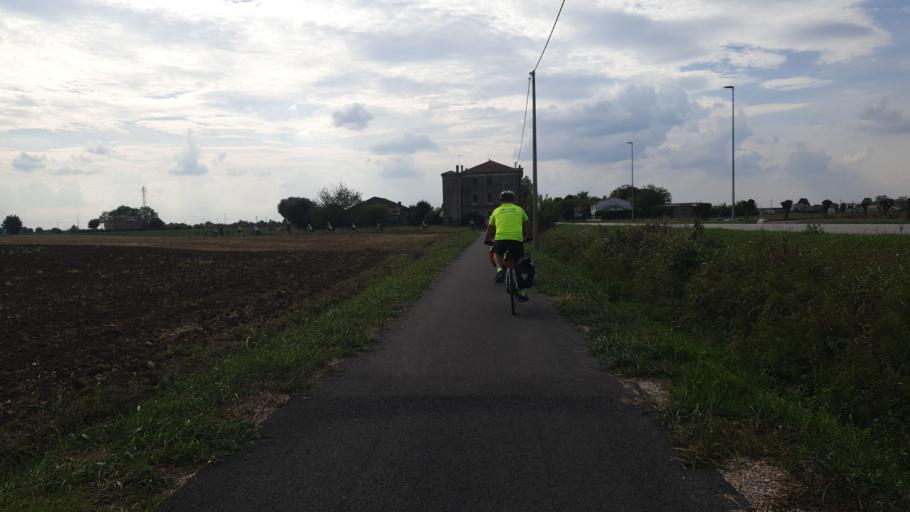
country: IT
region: Veneto
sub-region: Provincia di Vicenza
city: Noventa Vicentina
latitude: 45.2862
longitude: 11.5291
